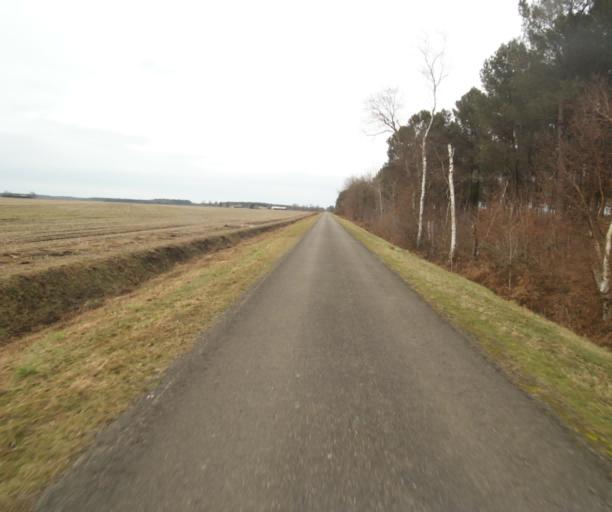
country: FR
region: Aquitaine
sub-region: Departement des Landes
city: Gabarret
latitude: 44.0325
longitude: -0.0641
